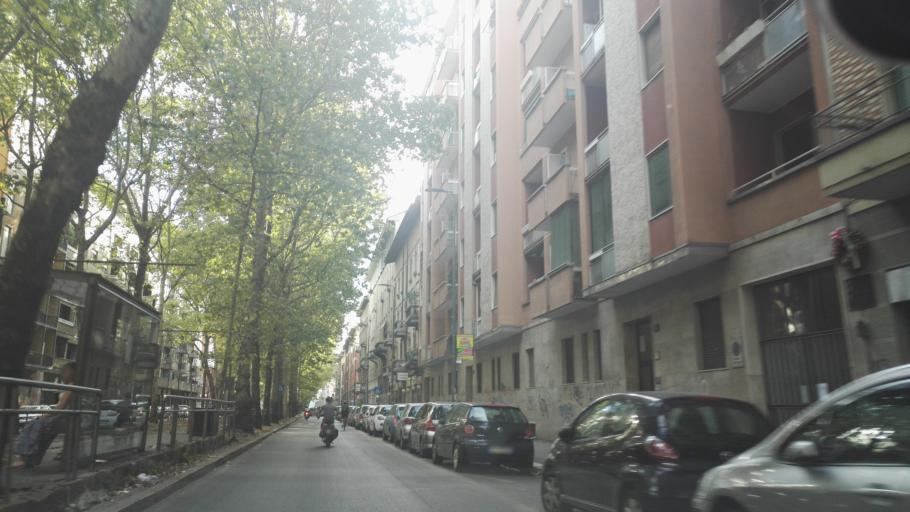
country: IT
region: Lombardy
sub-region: Citta metropolitana di Milano
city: Romano Banco
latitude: 45.4506
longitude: 9.1483
